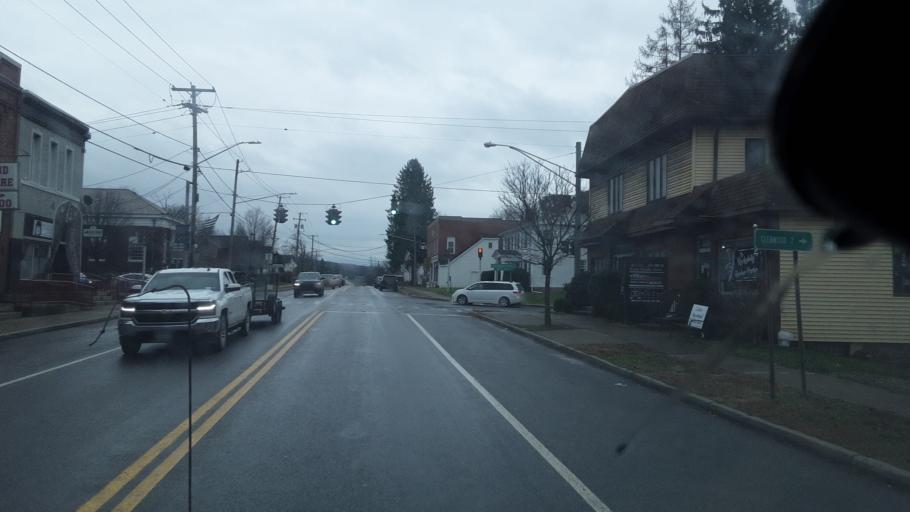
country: US
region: New York
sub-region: Erie County
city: Holland
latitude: 42.6415
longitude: -78.5425
